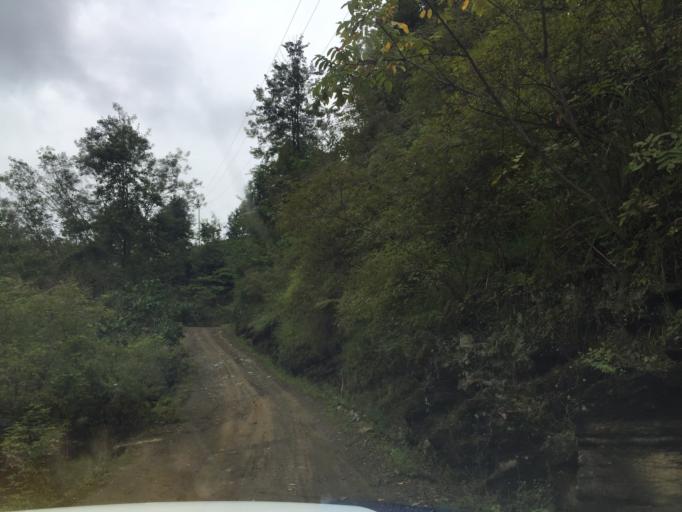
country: CN
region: Guizhou Sheng
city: Jingjiao
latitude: 28.3342
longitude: 108.1300
